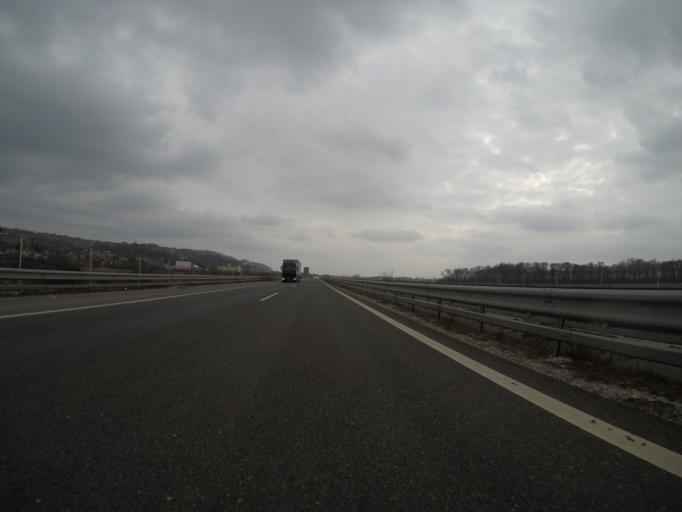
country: SI
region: Lendava-Lendva
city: Lendava
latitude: 46.5771
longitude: 16.4393
